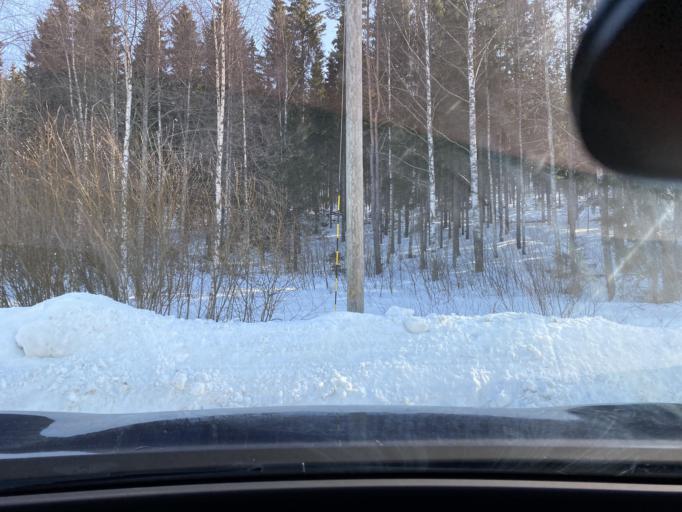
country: FI
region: Central Finland
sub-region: Jyvaeskylae
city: Muurame
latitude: 62.0934
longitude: 25.6427
